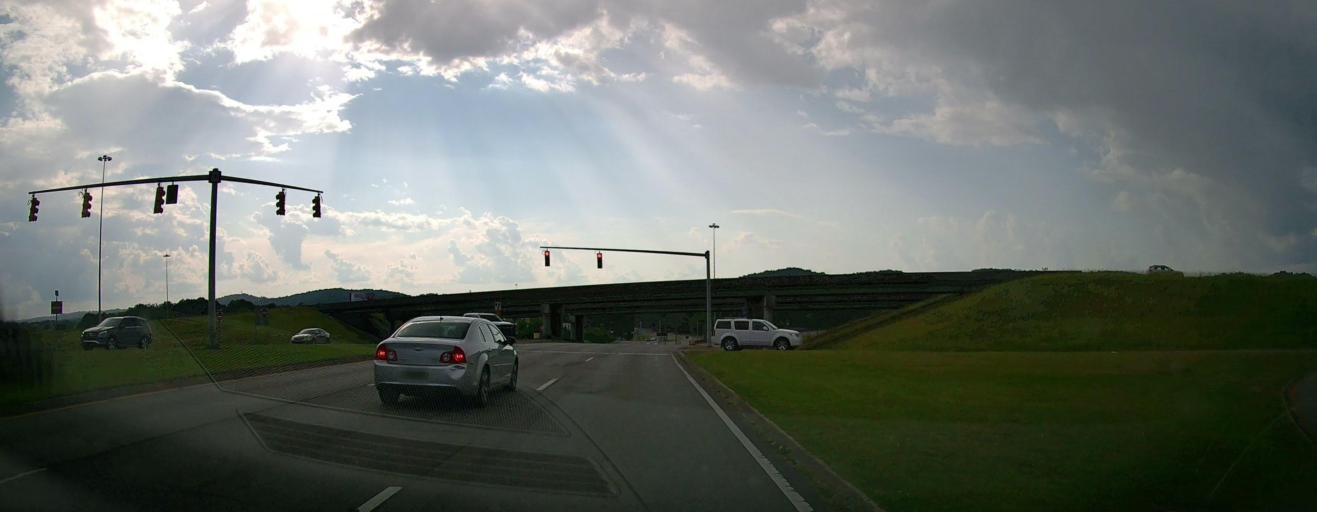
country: US
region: Alabama
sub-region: Jefferson County
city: Irondale
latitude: 33.5329
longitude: -86.6965
